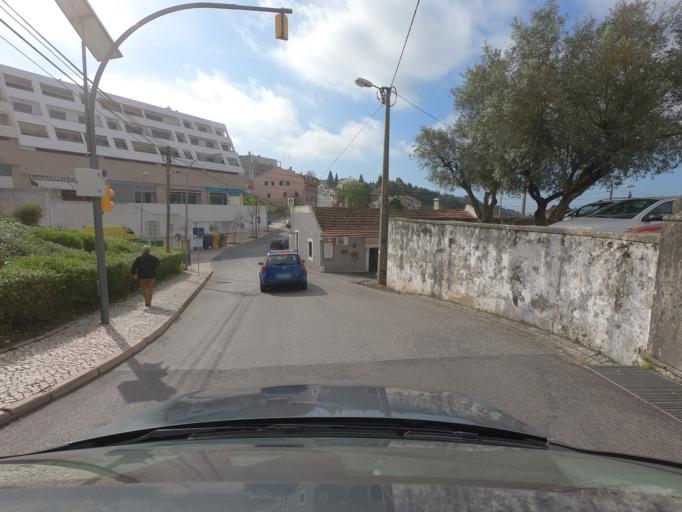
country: PT
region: Lisbon
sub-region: Oeiras
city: Barcarena
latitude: 38.7314
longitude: -9.2778
